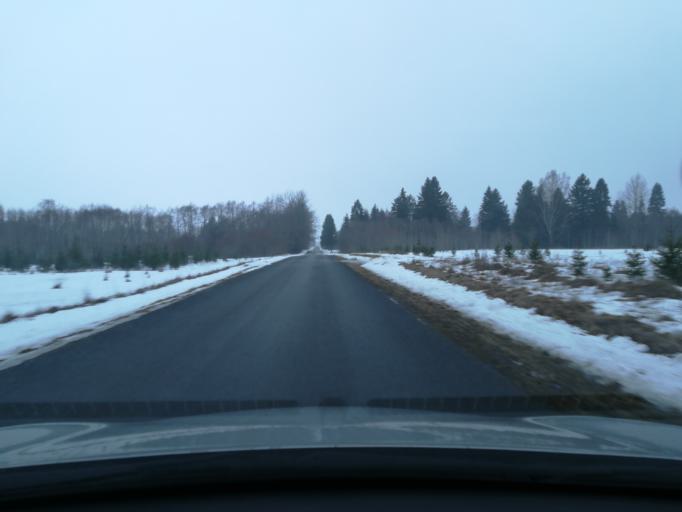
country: EE
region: Harju
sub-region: Raasiku vald
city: Raasiku
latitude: 59.3459
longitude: 25.2181
